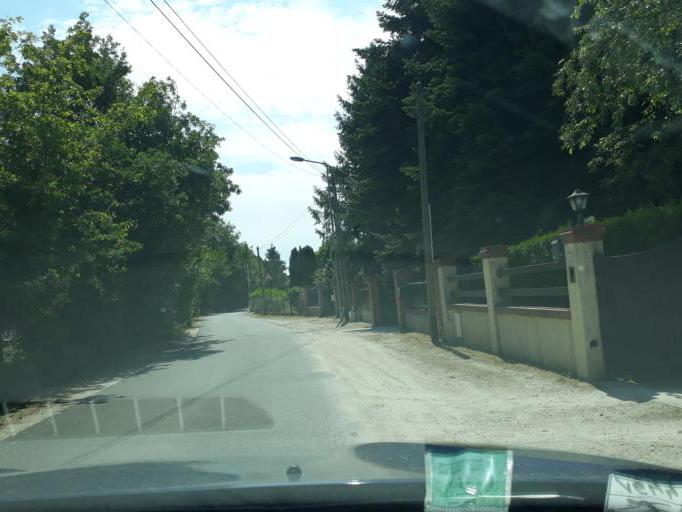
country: FR
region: Centre
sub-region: Departement du Loir-et-Cher
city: Vouzon
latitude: 47.6493
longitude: 2.0505
